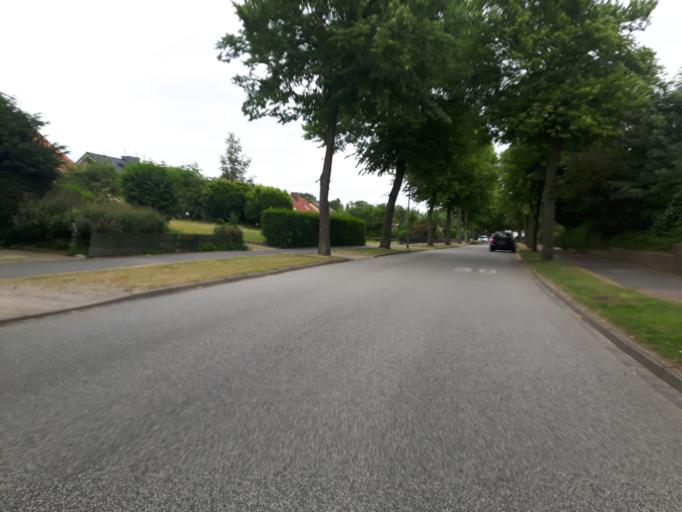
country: DE
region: Schleswig-Holstein
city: Neustadt in Holstein
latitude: 54.0917
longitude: 10.8519
